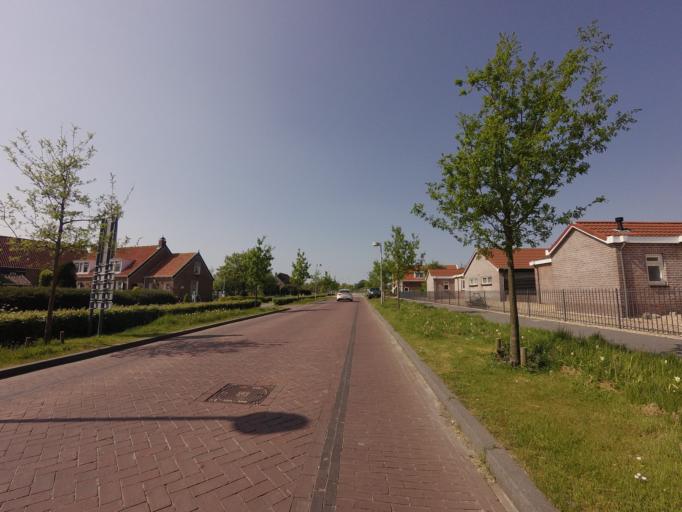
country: NL
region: Zeeland
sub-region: Gemeente Middelburg
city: Middelburg
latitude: 51.5540
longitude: 3.5871
